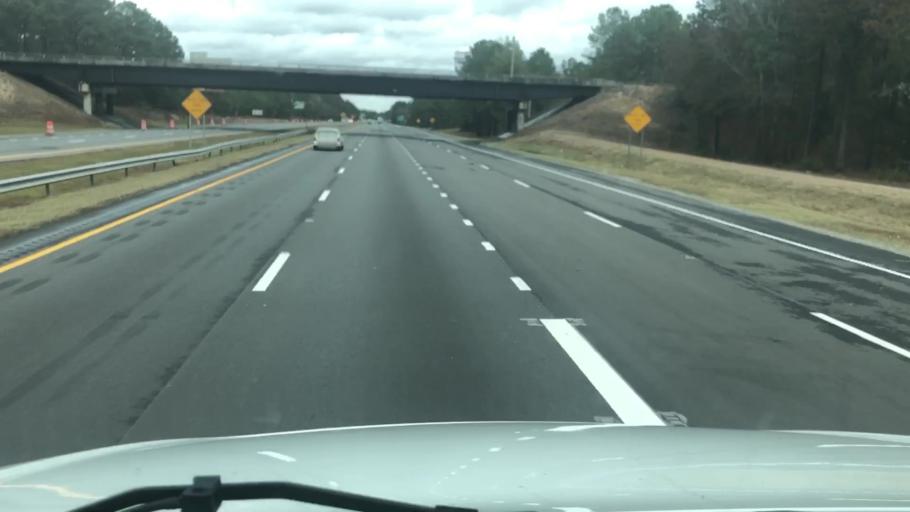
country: US
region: North Carolina
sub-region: Cumberland County
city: Eastover
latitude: 35.0948
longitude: -78.7777
